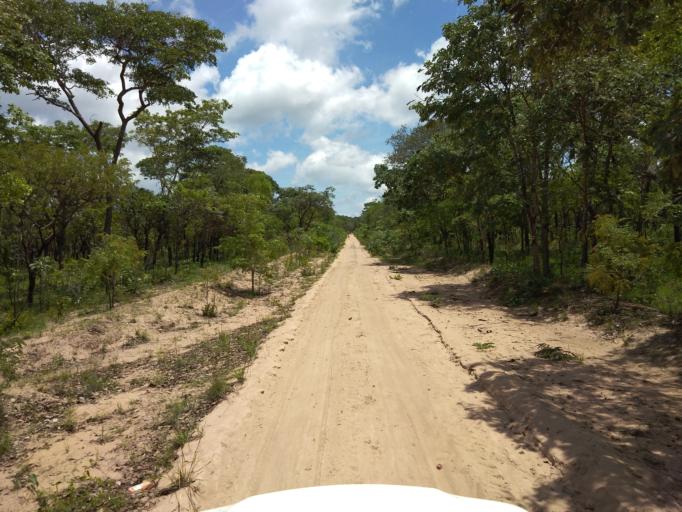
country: ZM
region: Central
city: Mkushi
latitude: -13.8979
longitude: 29.8568
